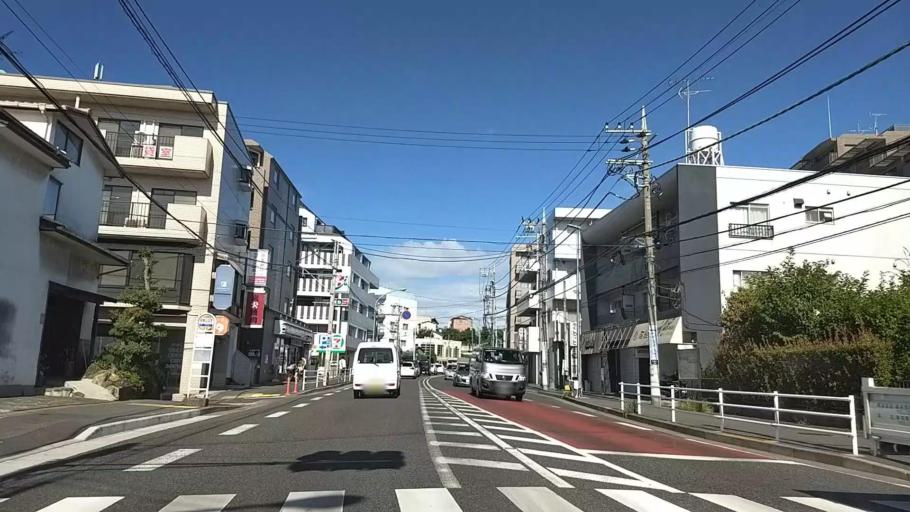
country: JP
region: Kanagawa
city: Yokohama
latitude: 35.4973
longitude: 139.6151
